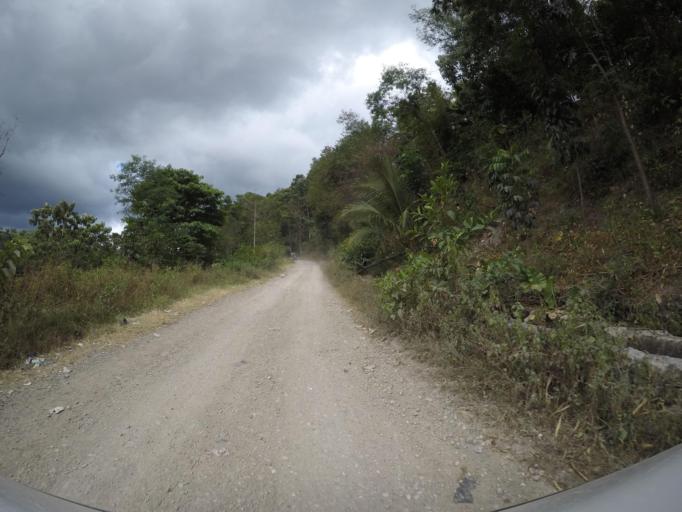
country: TL
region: Baucau
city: Baucau
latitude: -8.6274
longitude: 126.6564
